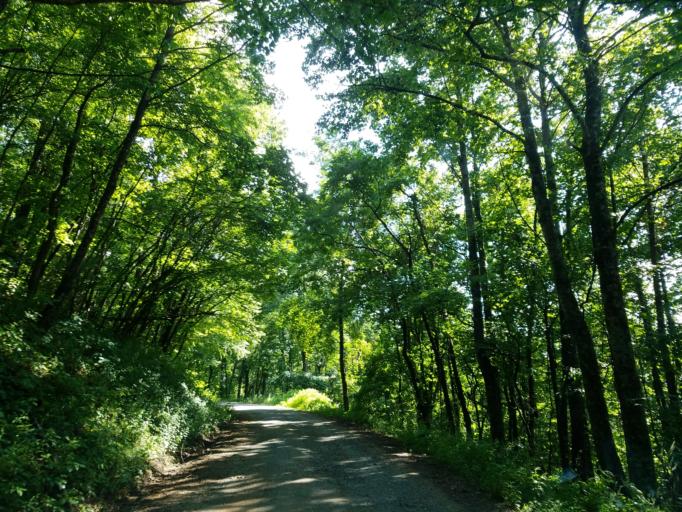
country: US
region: Georgia
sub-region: Fannin County
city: Blue Ridge
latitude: 34.6706
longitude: -84.2468
